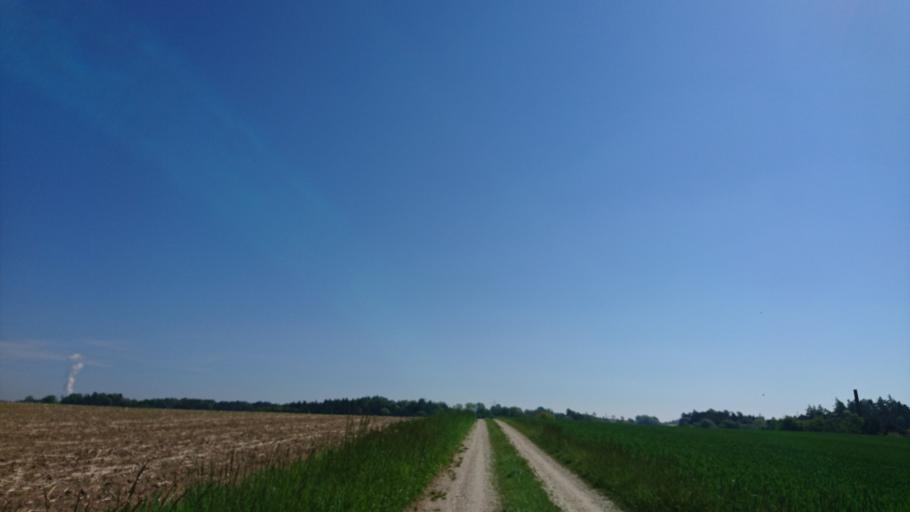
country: DE
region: Bavaria
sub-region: Lower Bavaria
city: Stallwang
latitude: 48.5307
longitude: 12.2267
